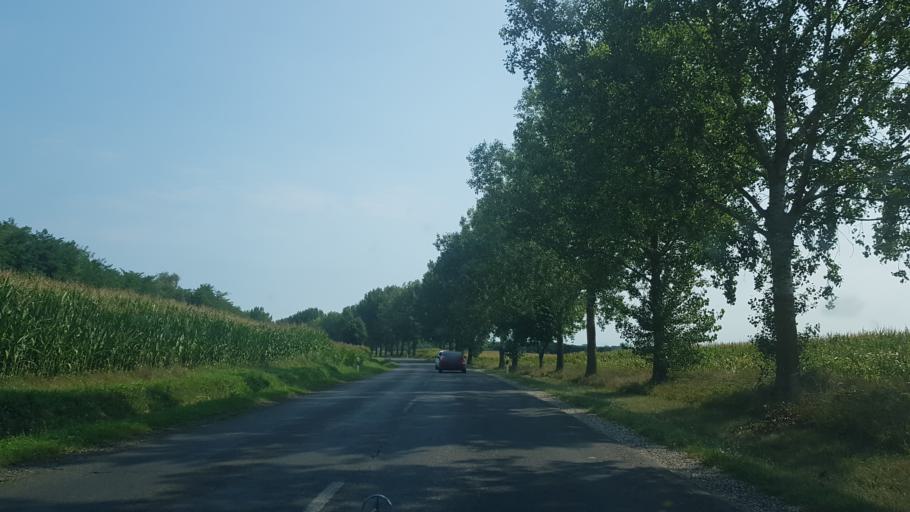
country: HU
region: Somogy
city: Segesd
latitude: 46.3624
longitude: 17.3494
